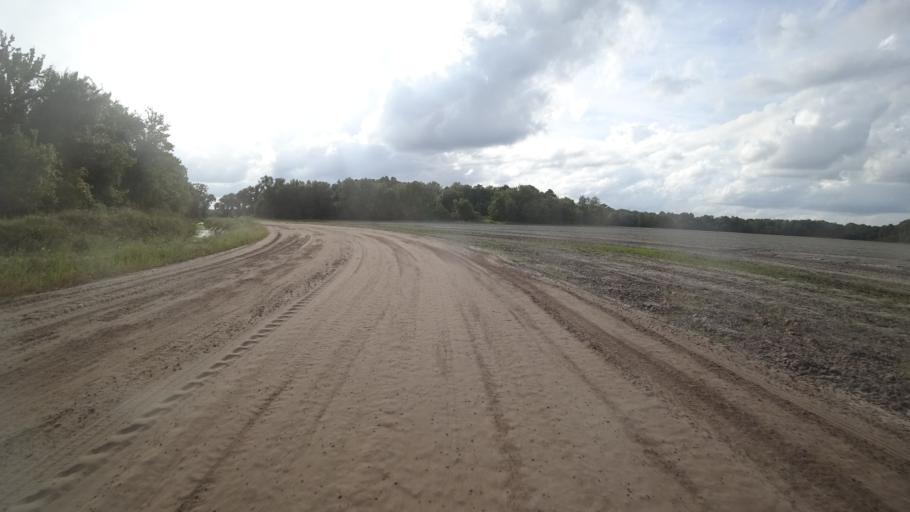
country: US
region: Florida
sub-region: Hillsborough County
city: Wimauma
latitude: 27.5978
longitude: -82.1375
